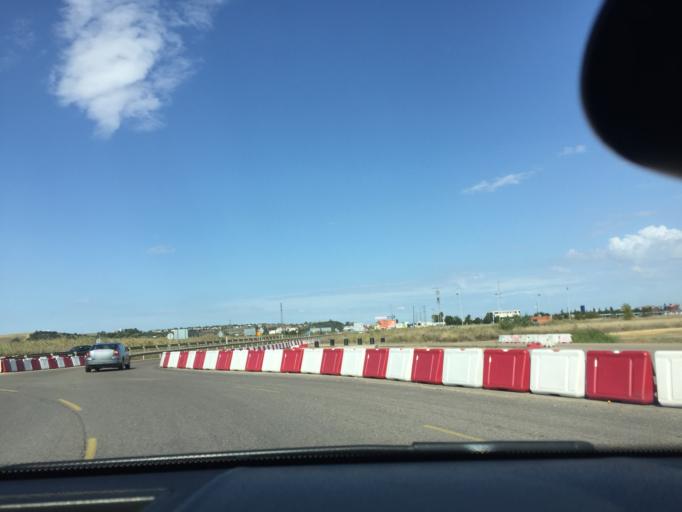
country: ES
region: Andalusia
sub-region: Provincia de Sevilla
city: Palomares del Rio
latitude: 37.3076
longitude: -6.0388
